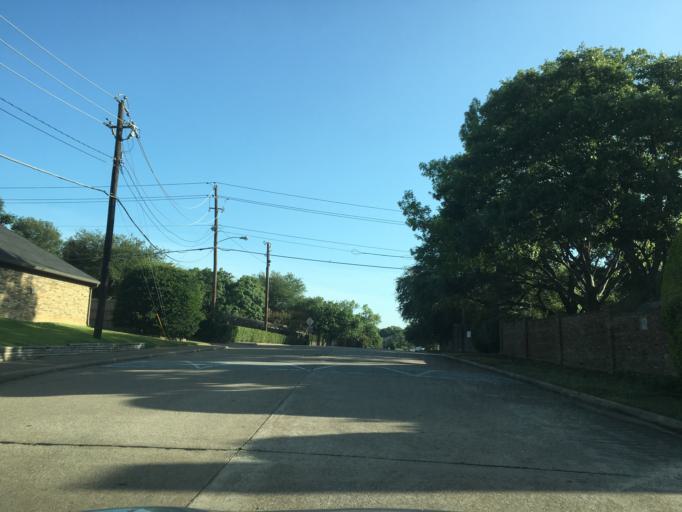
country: US
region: Texas
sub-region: Dallas County
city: Richardson
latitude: 32.8914
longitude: -96.7368
